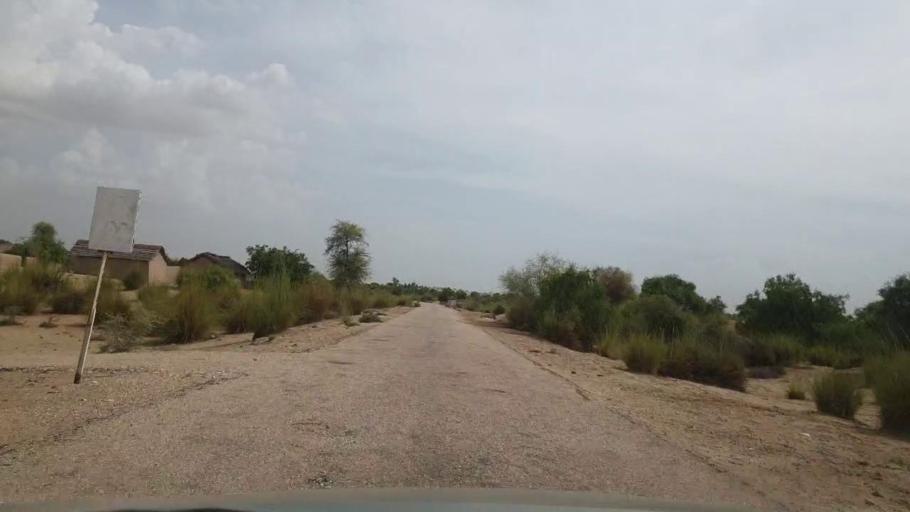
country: PK
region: Sindh
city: Bozdar
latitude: 27.0885
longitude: 69.0139
